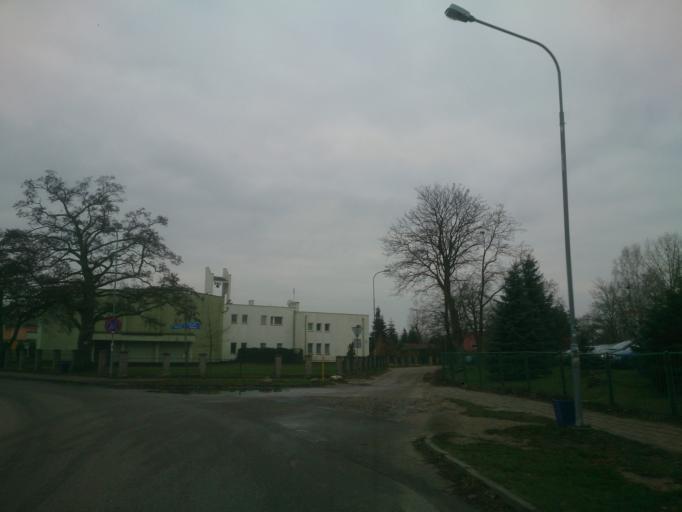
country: PL
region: West Pomeranian Voivodeship
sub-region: Powiat slawienski
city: Darlowo
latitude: 54.3825
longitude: 16.3192
